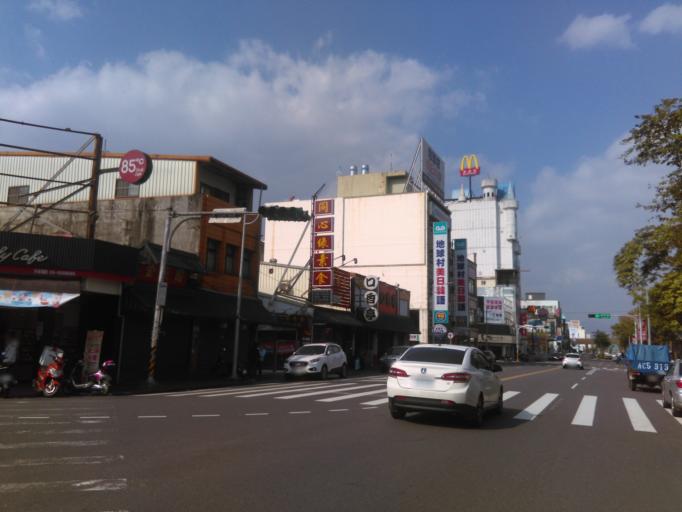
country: TW
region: Taiwan
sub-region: Yilan
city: Yilan
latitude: 24.7554
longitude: 121.7579
